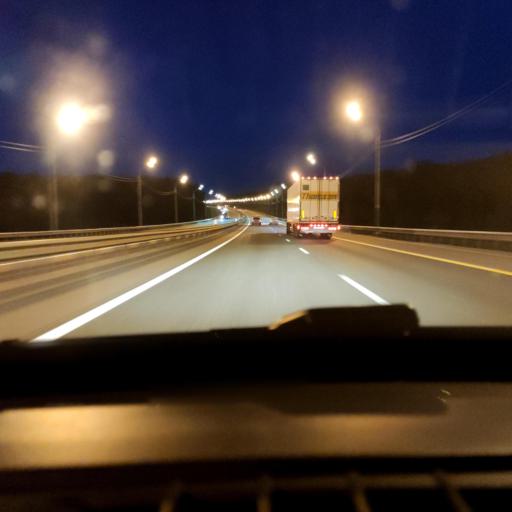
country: RU
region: Lipetsk
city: Khlevnoye
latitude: 52.2251
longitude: 39.1048
